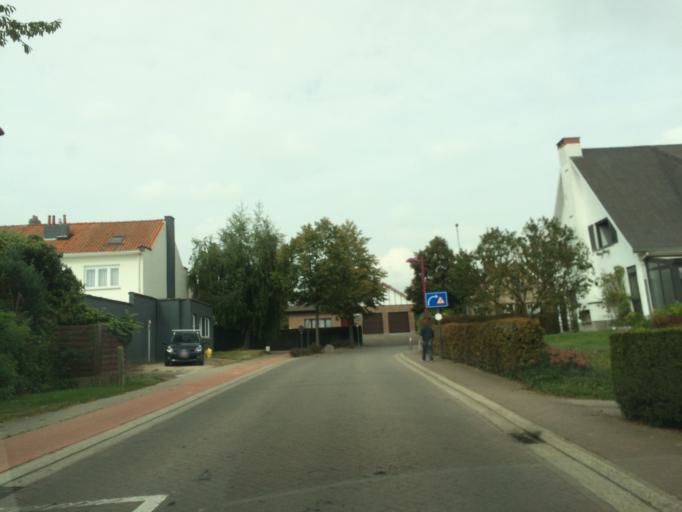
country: BE
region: Flanders
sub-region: Provincie Vlaams-Brabant
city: Wemmel
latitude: 50.8987
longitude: 4.2772
